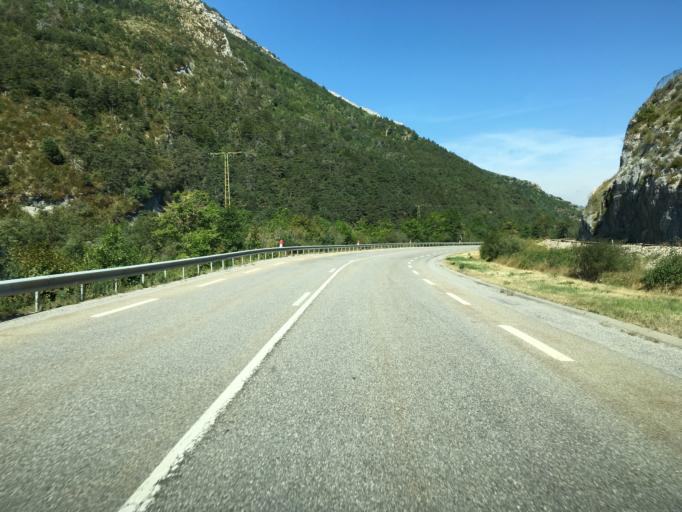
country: FR
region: Provence-Alpes-Cote d'Azur
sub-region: Departement des Hautes-Alpes
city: Veynes
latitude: 44.5773
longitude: 5.7256
